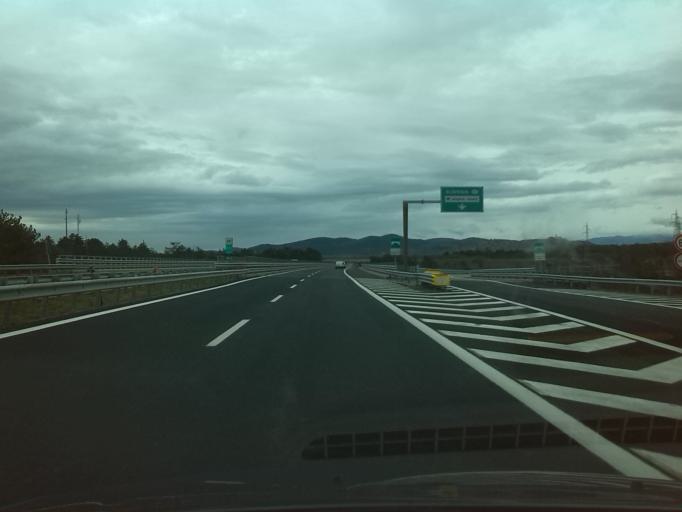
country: IT
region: Friuli Venezia Giulia
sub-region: Provincia di Trieste
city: Villa Opicina
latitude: 45.6884
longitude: 13.8102
